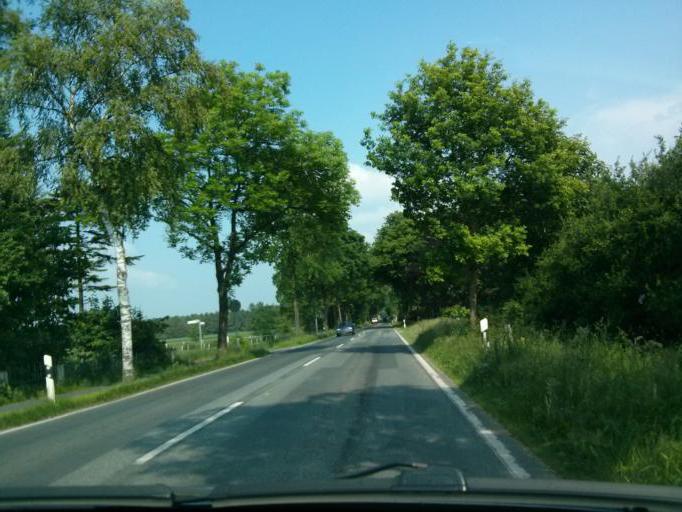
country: DE
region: Lower Saxony
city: Schiffdorf
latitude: 53.5151
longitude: 8.7020
